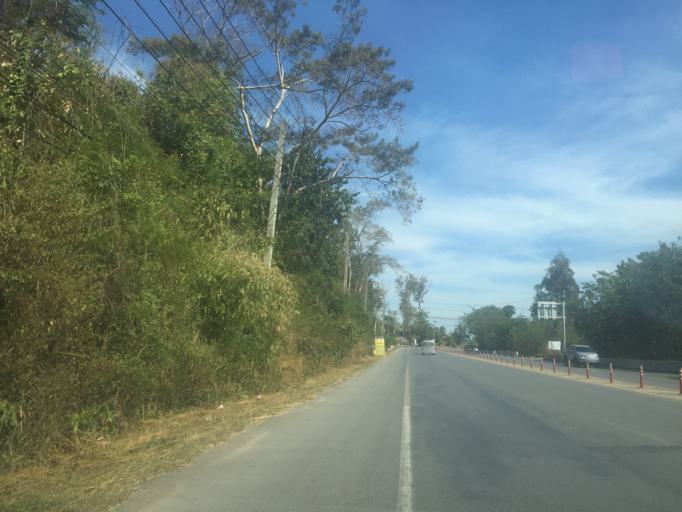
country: TH
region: Changwat Nong Bua Lamphu
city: Nong Bua Lamphu
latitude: 17.2423
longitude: 102.5177
